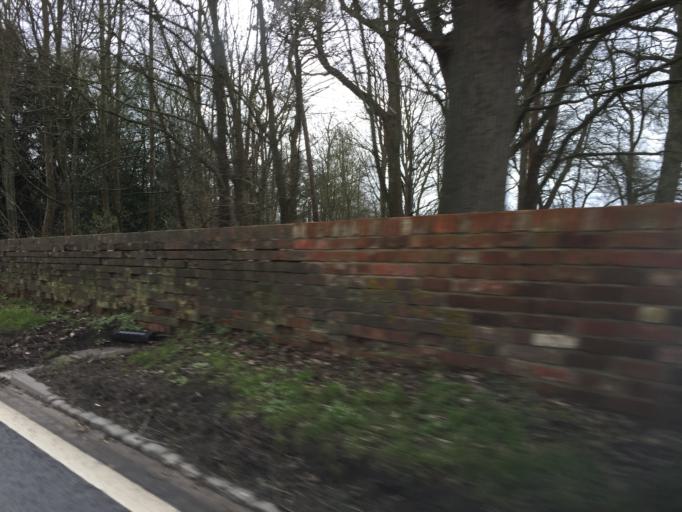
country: GB
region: England
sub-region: West Berkshire
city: Theale
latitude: 51.4412
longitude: -1.0922
